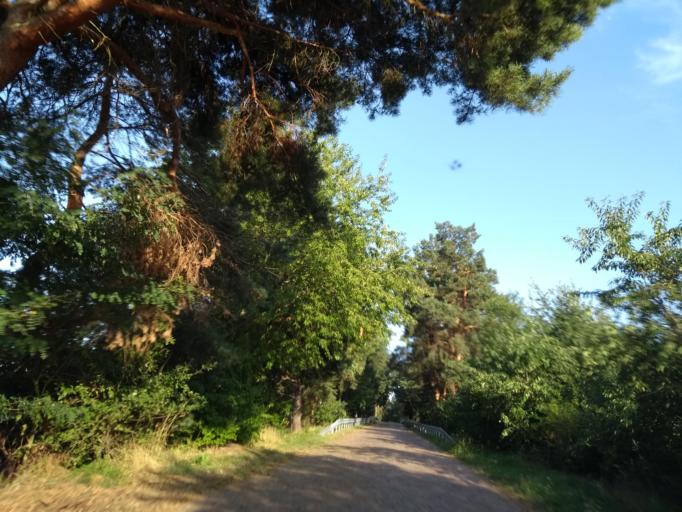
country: DE
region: Brandenburg
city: Lubbenau
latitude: 51.8398
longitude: 13.9173
